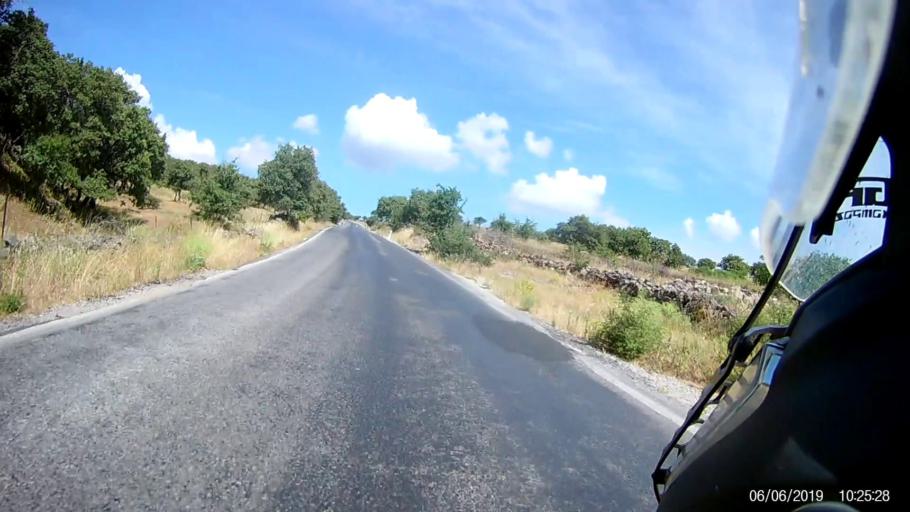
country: TR
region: Canakkale
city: Behram
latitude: 39.5060
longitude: 26.3953
